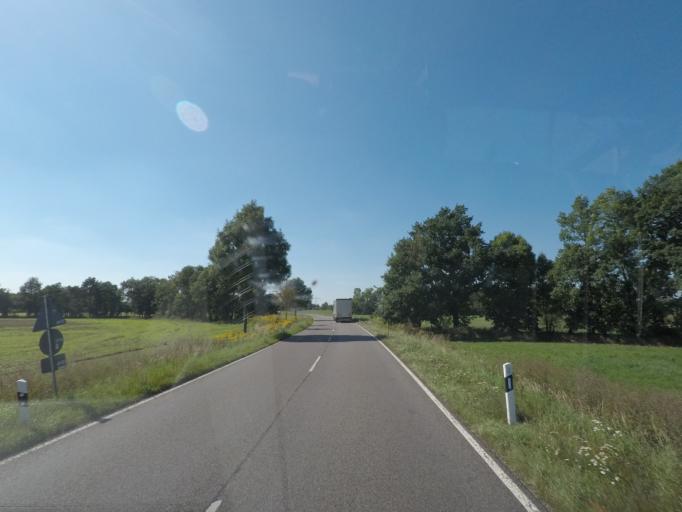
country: DE
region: Brandenburg
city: Grossraschen
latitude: 51.5746
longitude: 14.0906
